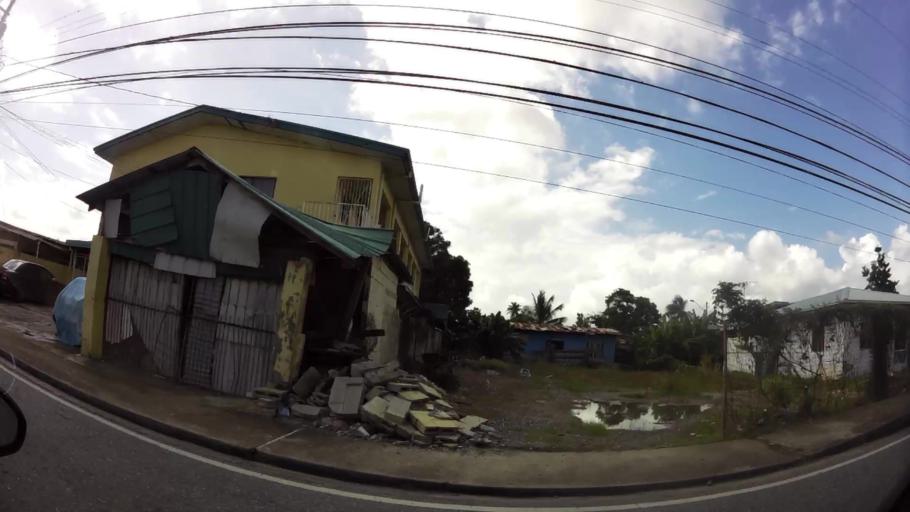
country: TT
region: Borough of Arima
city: Arima
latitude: 10.6317
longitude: -61.2759
